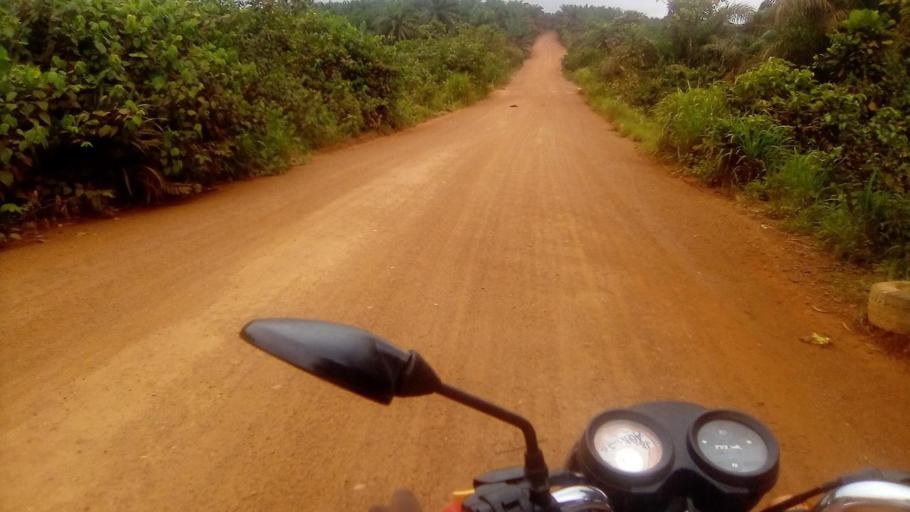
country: SL
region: Southern Province
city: Tongole
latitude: 7.4322
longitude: -11.8537
